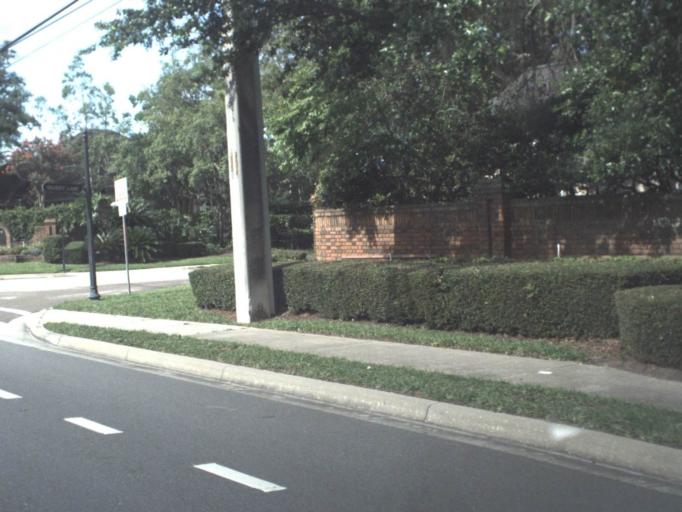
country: US
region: Florida
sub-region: Duval County
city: Jacksonville
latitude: 30.2300
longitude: -81.6169
